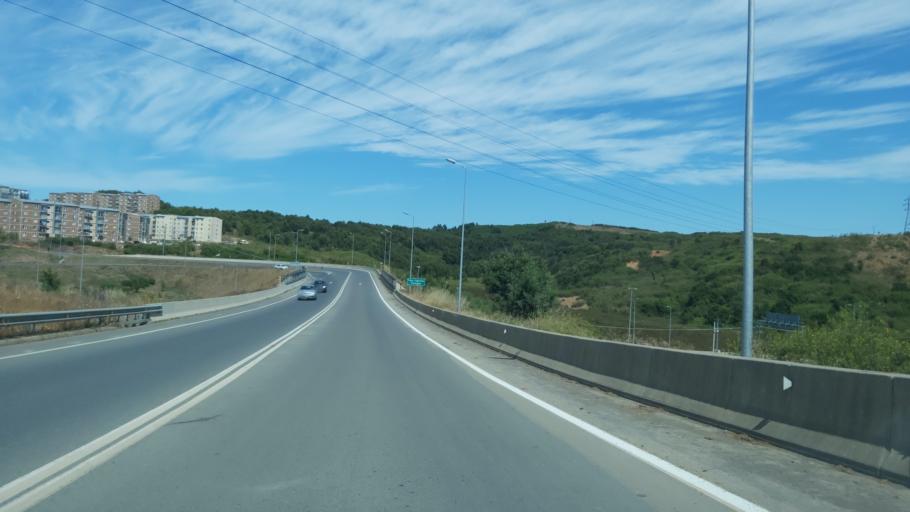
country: CL
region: Biobio
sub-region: Provincia de Concepcion
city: Coronel
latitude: -37.0238
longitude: -73.1340
